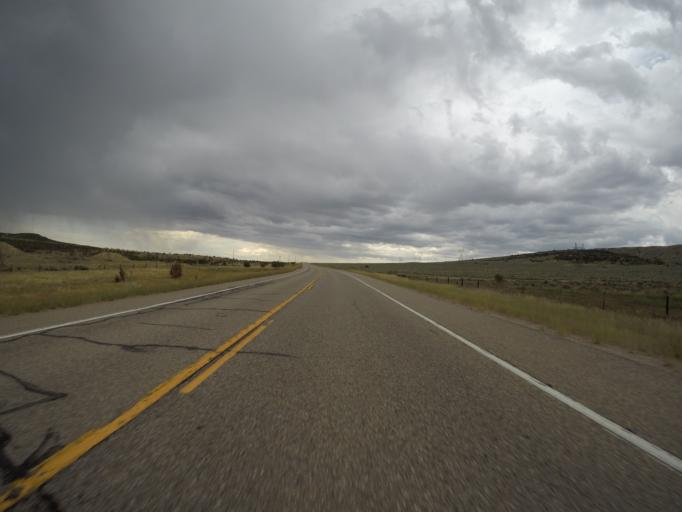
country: US
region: Colorado
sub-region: Rio Blanco County
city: Rangely
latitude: 40.3691
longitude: -108.3920
